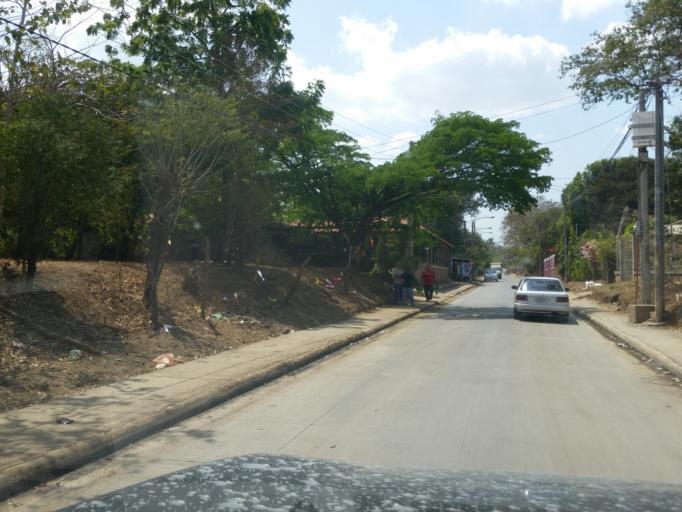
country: NI
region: Masaya
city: Ticuantepe
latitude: 12.0684
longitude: -86.2008
